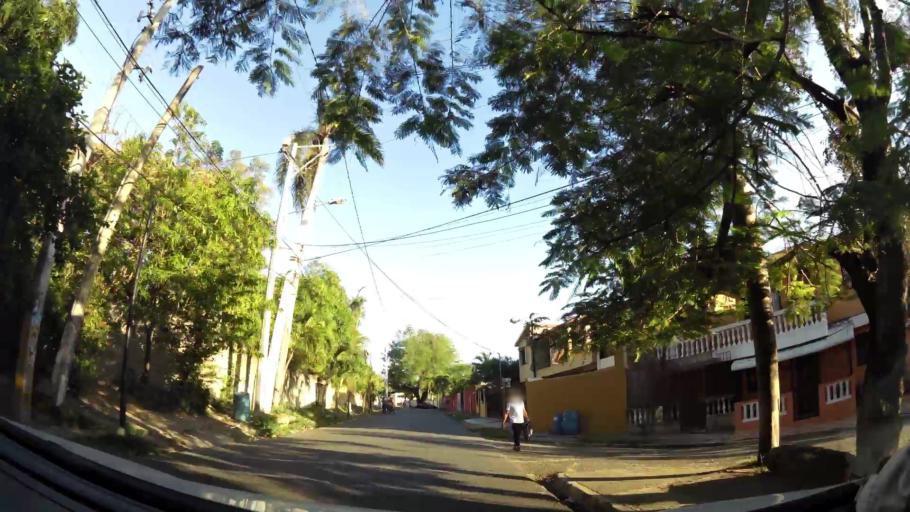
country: DO
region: Nacional
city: Santo Domingo
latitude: 18.4887
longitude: -69.9658
